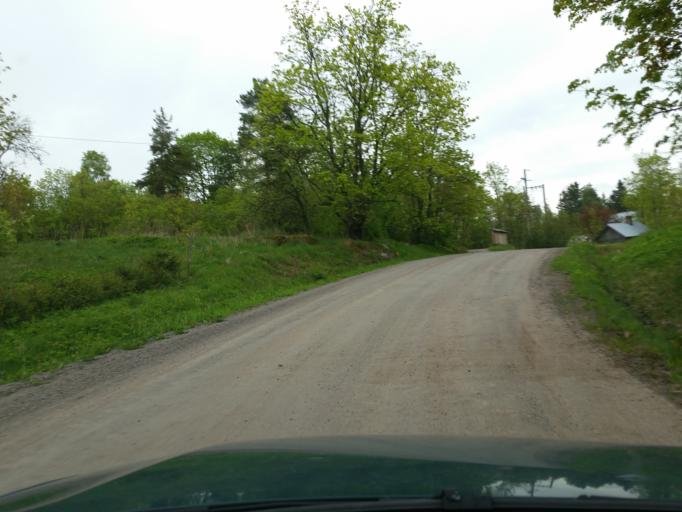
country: FI
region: Uusimaa
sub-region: Helsinki
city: Karjalohja
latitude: 60.1873
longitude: 23.6852
